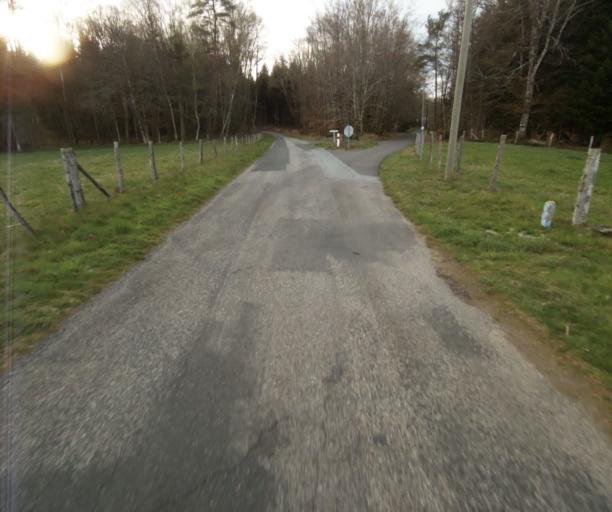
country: FR
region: Limousin
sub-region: Departement de la Correze
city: Argentat
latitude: 45.2179
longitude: 1.9574
